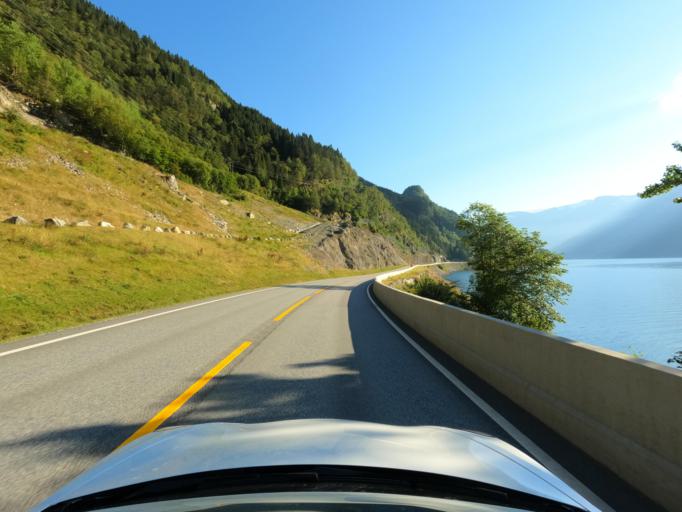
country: NO
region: Hordaland
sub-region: Ullensvang
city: Kinsarvik
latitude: 60.2959
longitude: 6.6394
